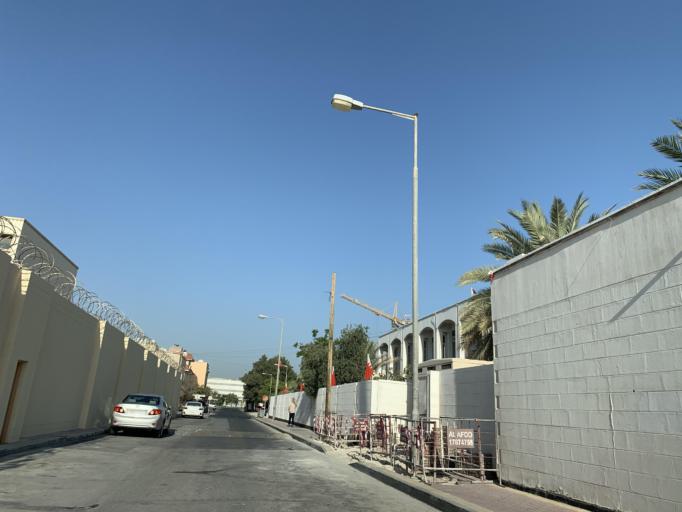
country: BH
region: Muharraq
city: Al Muharraq
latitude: 26.2621
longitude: 50.6058
